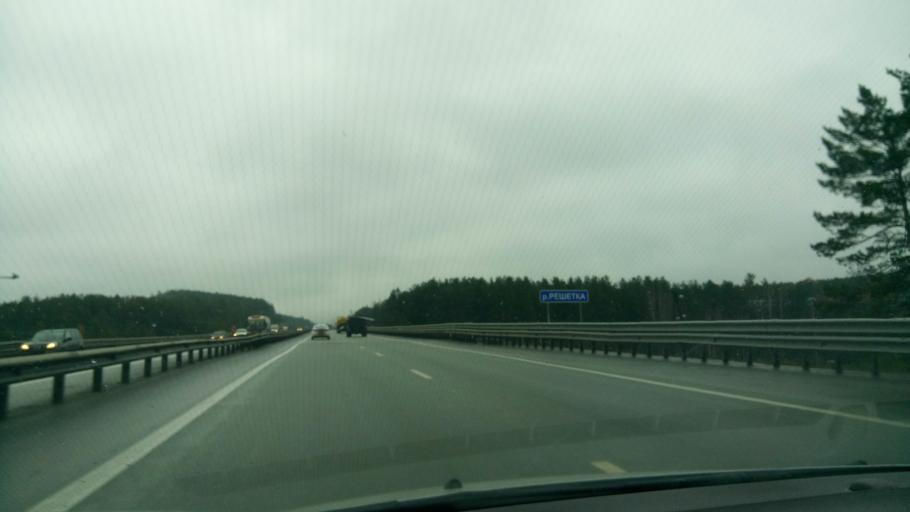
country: RU
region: Sverdlovsk
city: Severka
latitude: 56.8438
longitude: 60.2384
